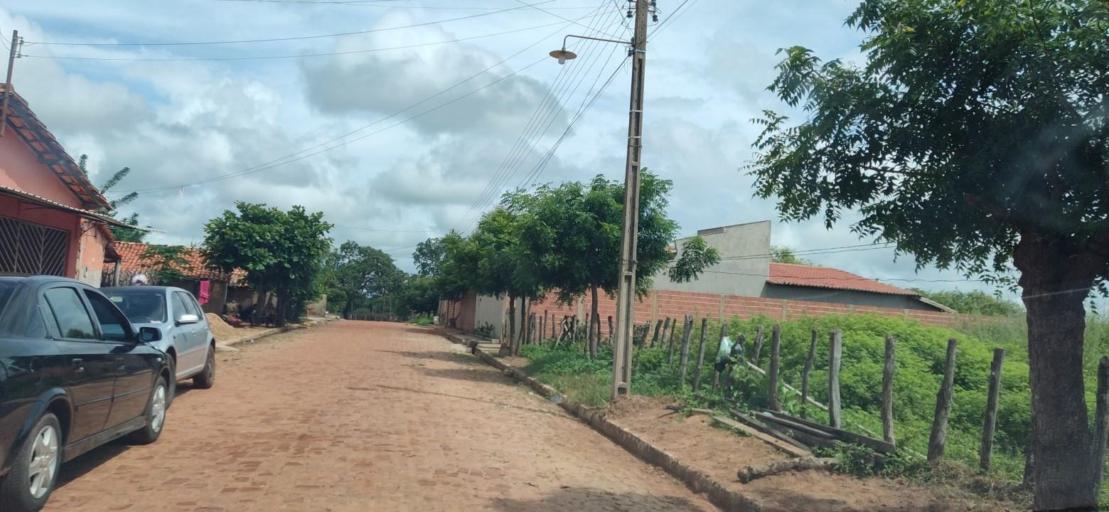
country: BR
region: Piaui
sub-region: Valenca Do Piaui
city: Valenca do Piaui
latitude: -6.1103
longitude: -41.7987
